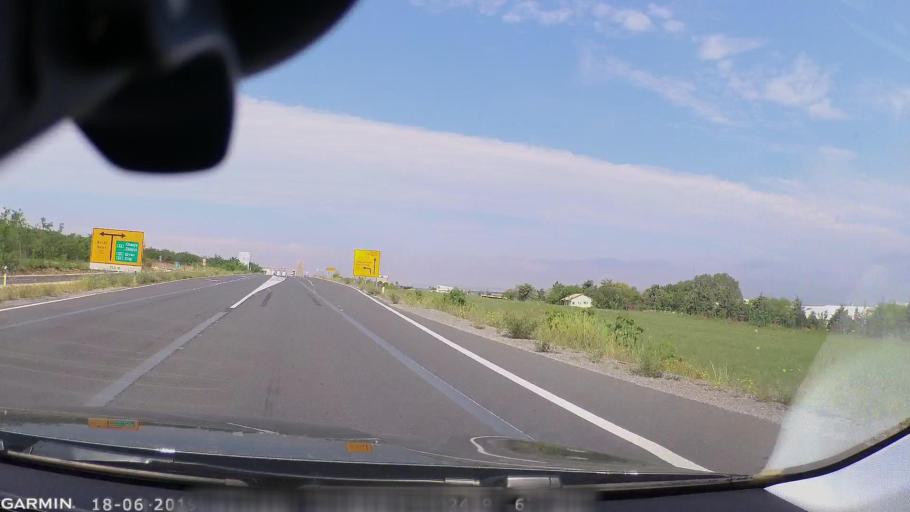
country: MK
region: Sveti Nikole
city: Sveti Nikole
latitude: 41.8258
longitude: 22.0079
